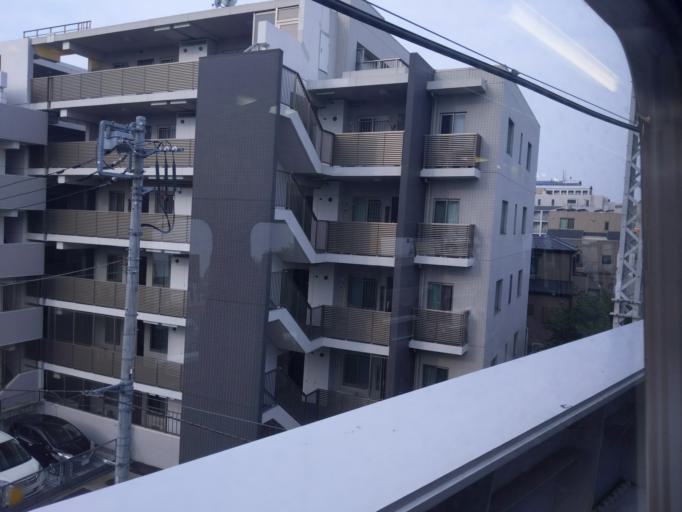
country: JP
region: Saitama
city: Kawaguchi
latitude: 35.7786
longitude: 139.6904
